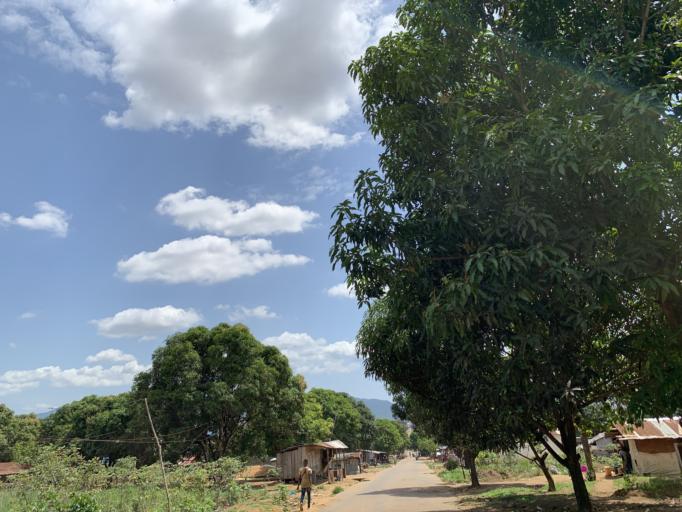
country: SL
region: Western Area
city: Waterloo
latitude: 8.3313
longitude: -13.0444
